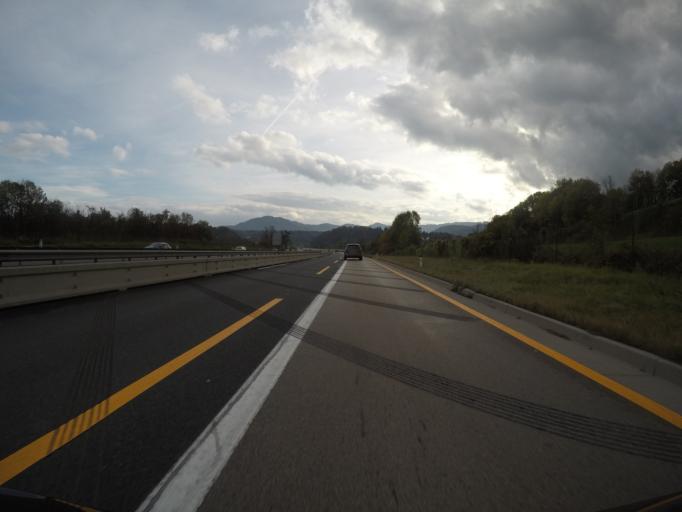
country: SI
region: Naklo
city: Naklo
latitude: 46.2969
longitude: 14.2838
